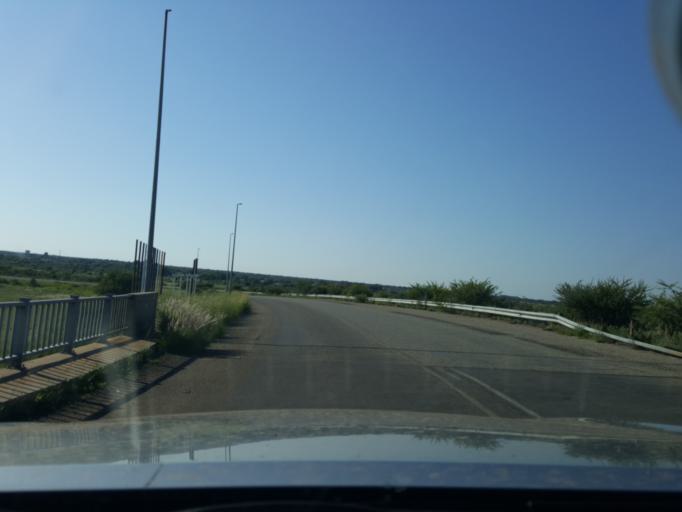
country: ZA
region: North-West
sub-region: Ngaka Modiri Molema District Municipality
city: Mahikeng
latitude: -25.8512
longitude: 25.6790
